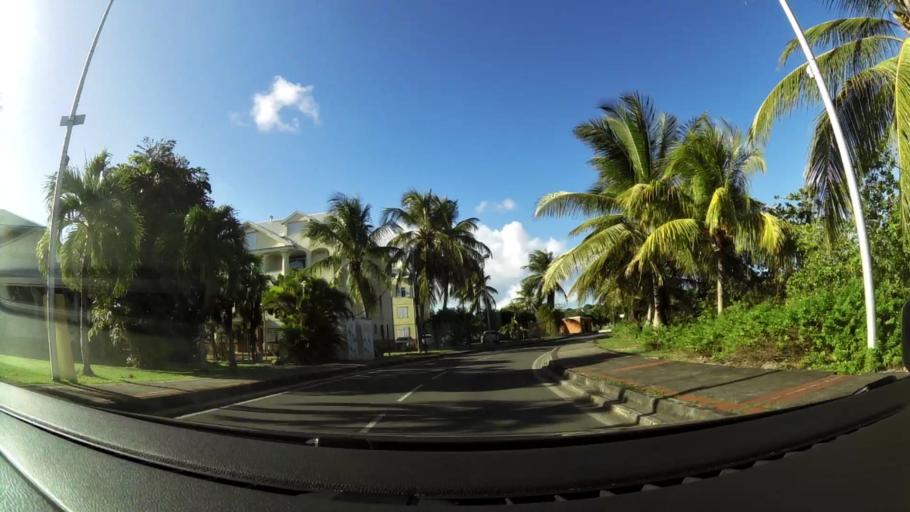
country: GP
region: Guadeloupe
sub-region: Guadeloupe
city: Le Gosier
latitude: 16.2086
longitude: -61.5059
